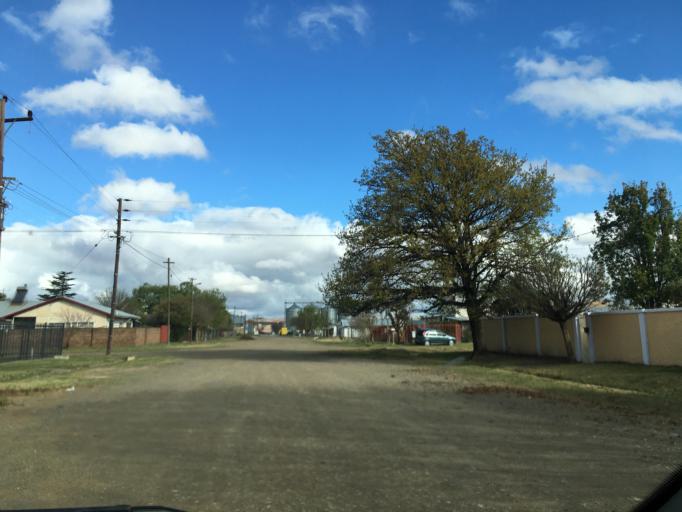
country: ZA
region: Eastern Cape
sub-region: Chris Hani District Municipality
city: Elliot
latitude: -31.3315
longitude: 27.8456
